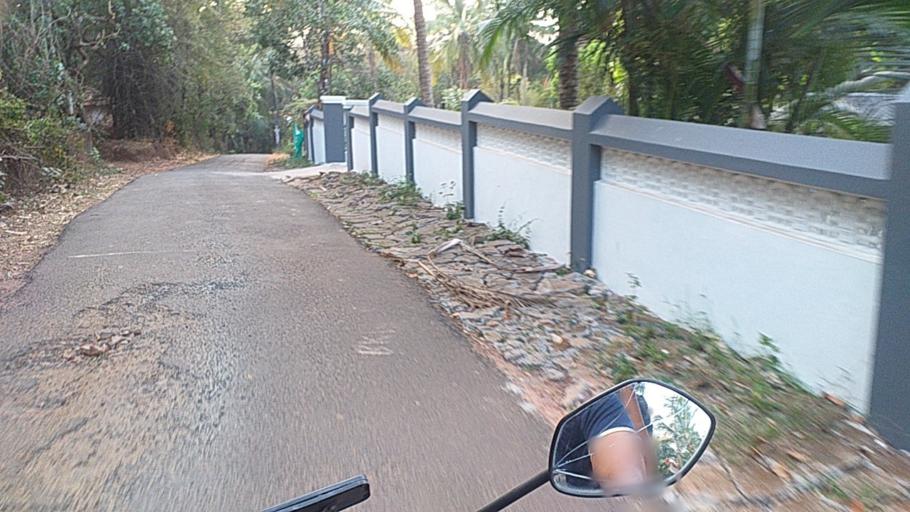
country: IN
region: Kerala
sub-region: Thrissur District
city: Kunnamkulam
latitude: 10.7380
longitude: 76.0438
